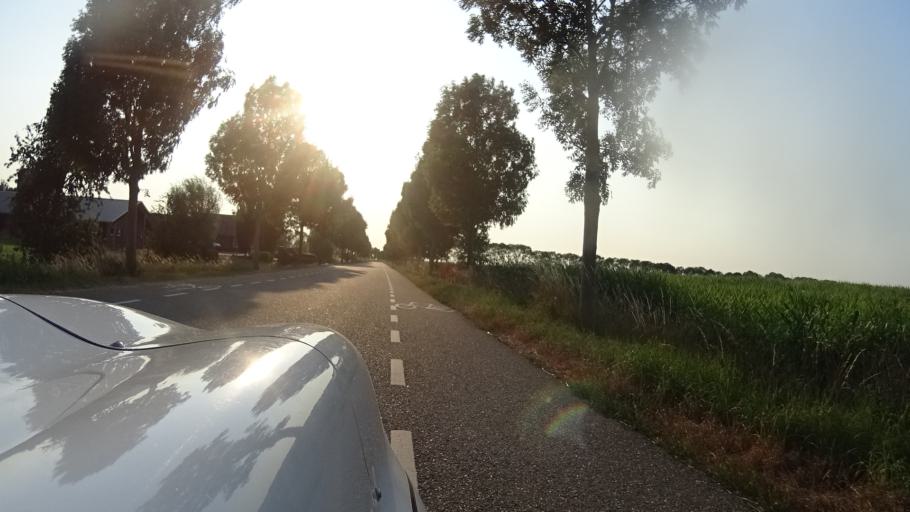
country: NL
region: Gelderland
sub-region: Gemeente Druten
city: Druten
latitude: 51.8444
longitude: 5.5509
